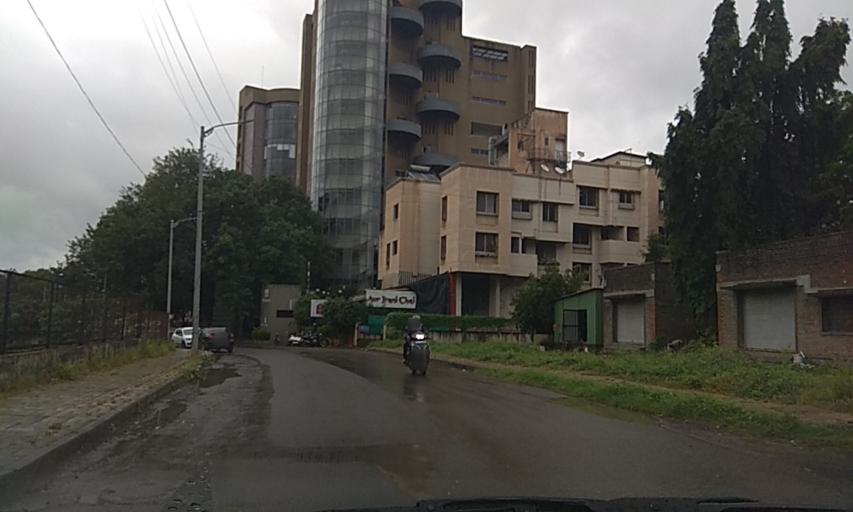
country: IN
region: Maharashtra
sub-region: Pune Division
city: Khadki
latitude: 18.5559
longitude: 73.7994
